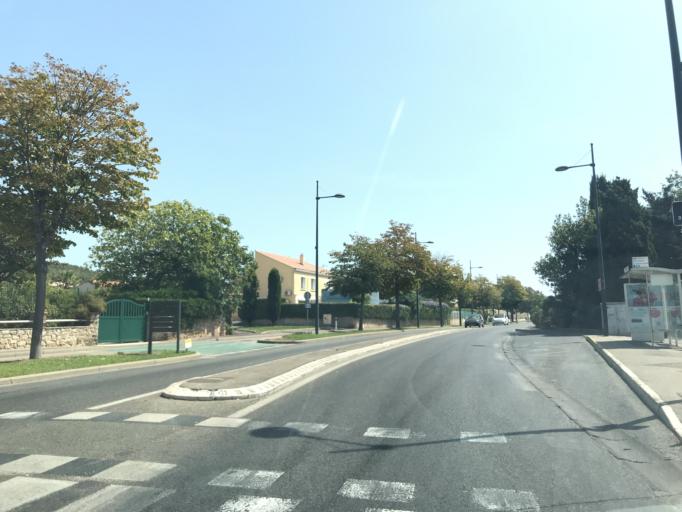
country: FR
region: Provence-Alpes-Cote d'Azur
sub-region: Departement du Var
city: Six-Fours-les-Plages
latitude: 43.0984
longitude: 5.8276
